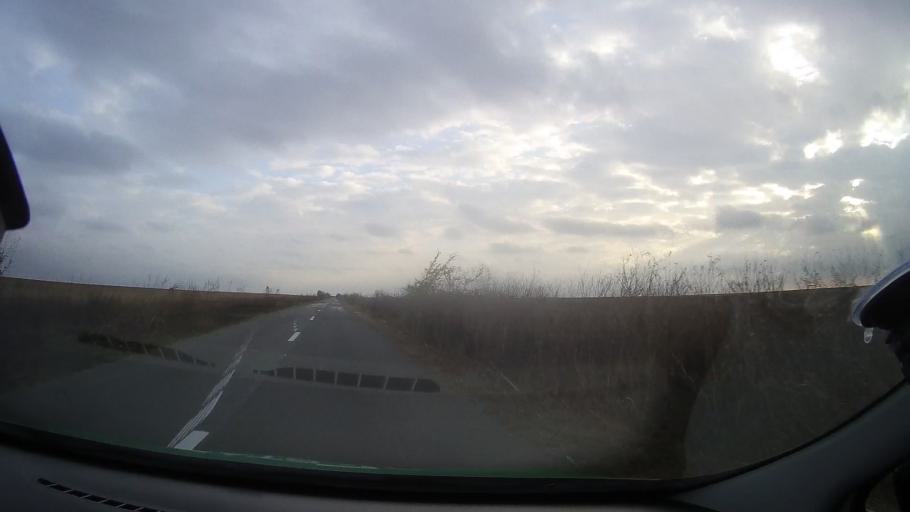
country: RO
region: Constanta
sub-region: Comuna Pestera
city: Pestera
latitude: 44.1400
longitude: 28.1173
